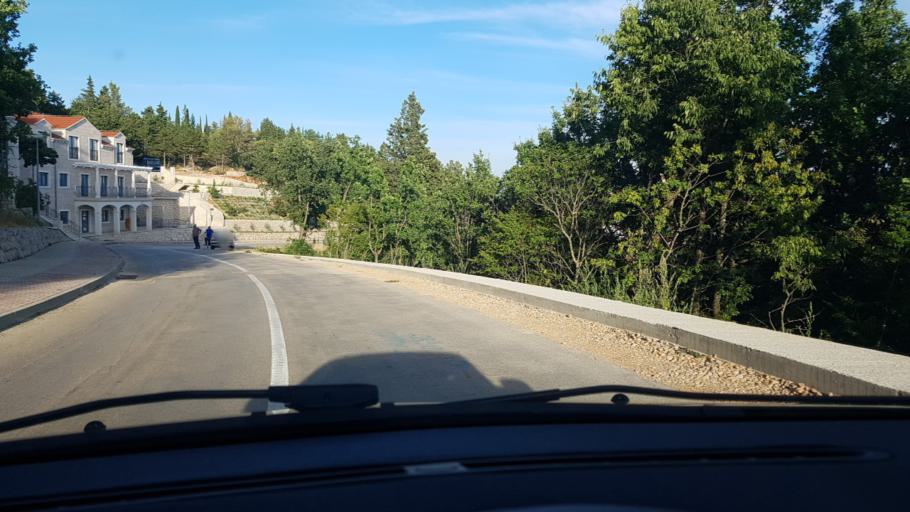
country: HR
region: Splitsko-Dalmatinska
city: Imotski
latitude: 43.4495
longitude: 17.2043
